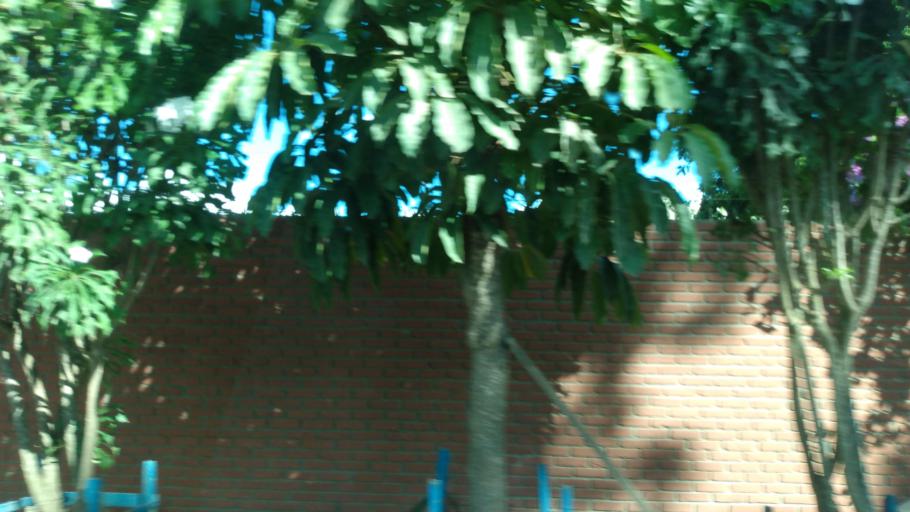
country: ET
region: Oromiya
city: Gore
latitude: 8.1967
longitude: 35.5653
